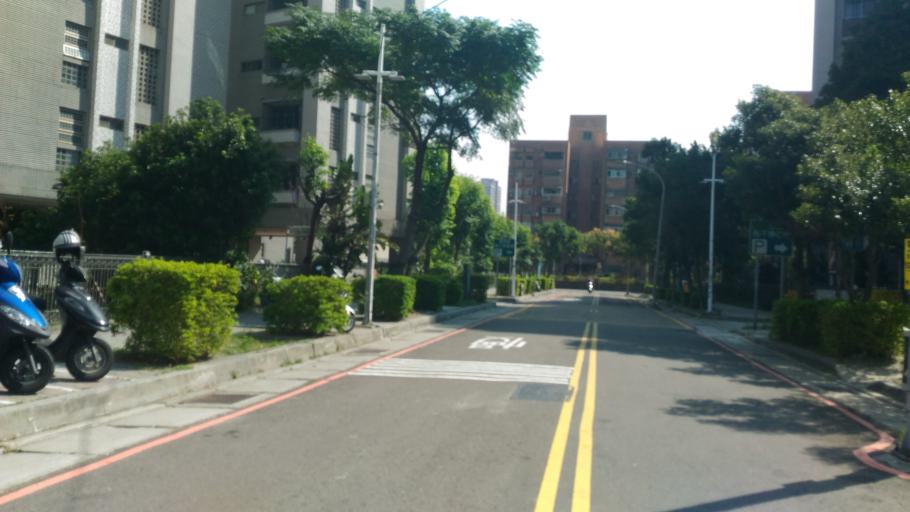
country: TW
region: Taiwan
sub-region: Hsinchu
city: Hsinchu
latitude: 24.8184
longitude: 120.9672
